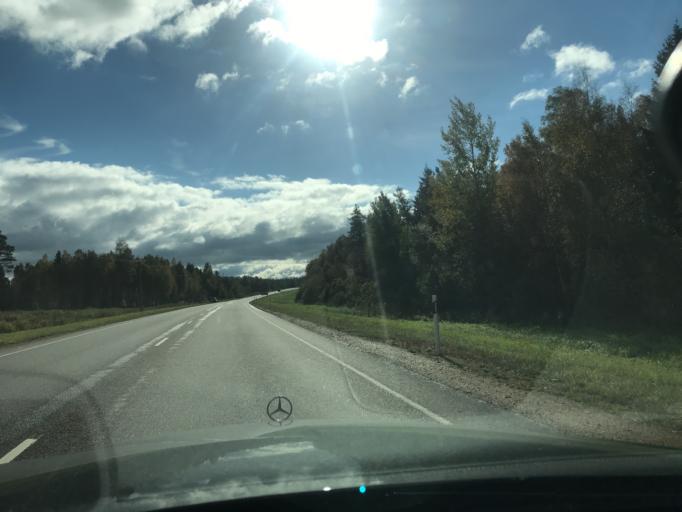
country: EE
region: Vorumaa
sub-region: Voru linn
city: Voru
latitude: 57.8344
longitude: 27.0607
